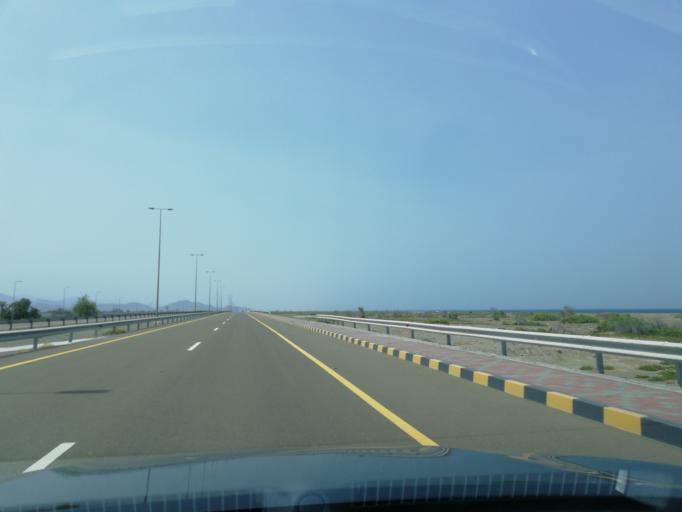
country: OM
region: Al Batinah
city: Shinas
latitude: 24.8934
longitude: 56.3999
